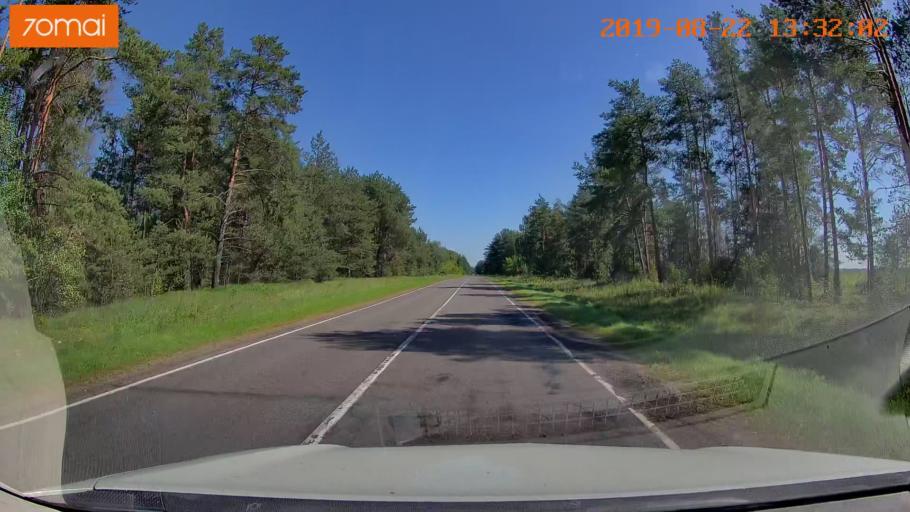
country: BY
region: Minsk
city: Staryya Darohi
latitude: 53.2172
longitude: 28.1941
